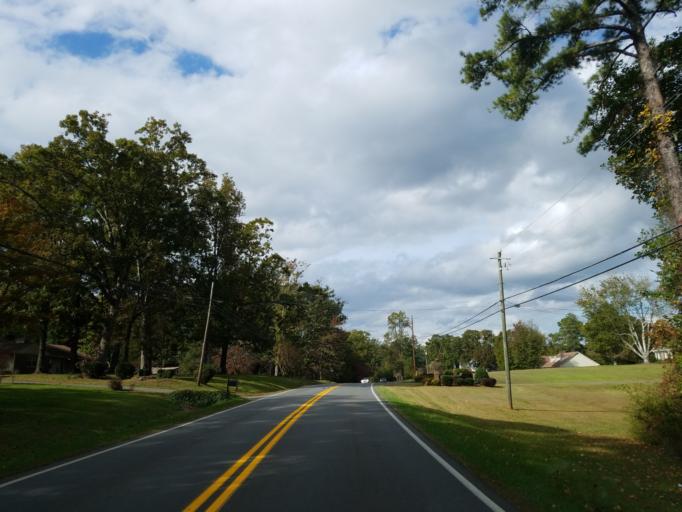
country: US
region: Georgia
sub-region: Pickens County
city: Jasper
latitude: 34.4501
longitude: -84.4238
